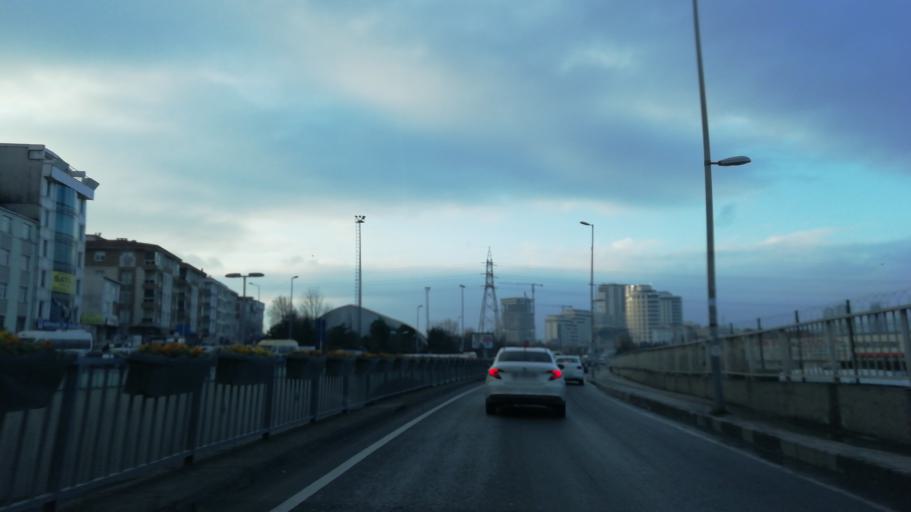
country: TR
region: Istanbul
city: Esenyurt
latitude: 41.0144
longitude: 28.6930
